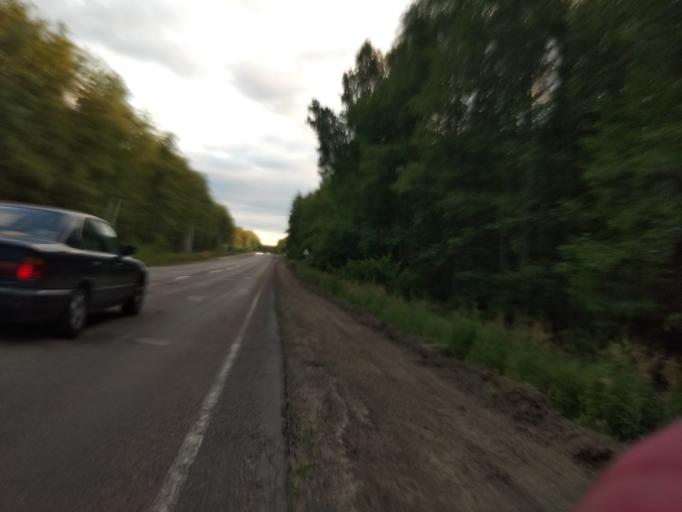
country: RU
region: Moskovskaya
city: Misheronskiy
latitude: 55.6363
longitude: 39.7486
